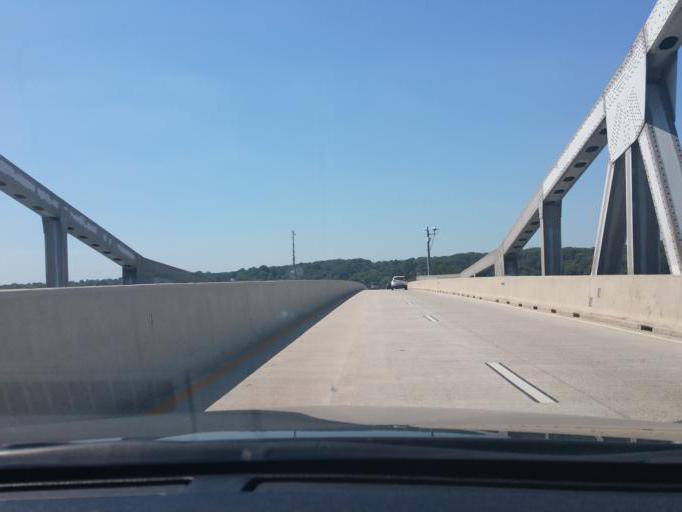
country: US
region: Maryland
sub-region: Harford County
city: Havre de Grace
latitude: 39.5602
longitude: -76.0910
